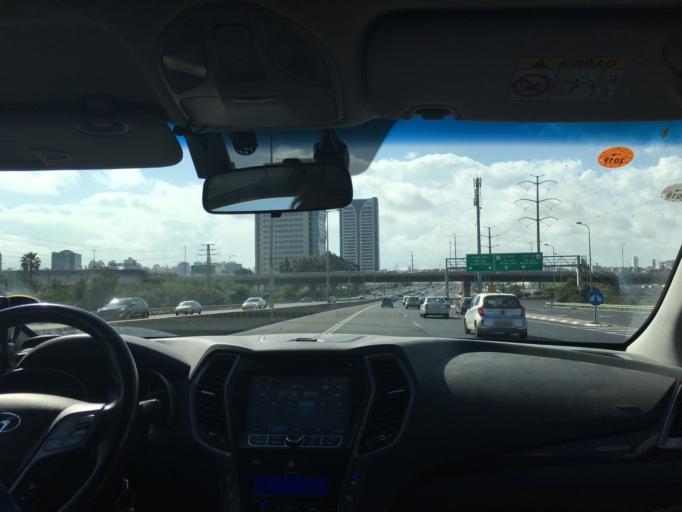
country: IL
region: Tel Aviv
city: Giv`at Shemu'el
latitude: 32.1023
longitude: 34.8482
